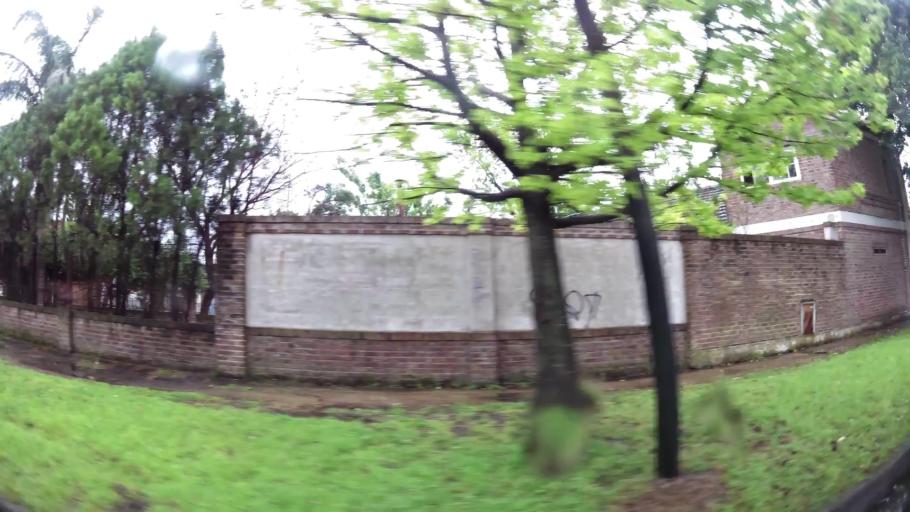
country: AR
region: Buenos Aires
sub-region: Partido de Lomas de Zamora
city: Lomas de Zamora
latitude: -34.7439
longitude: -58.3767
